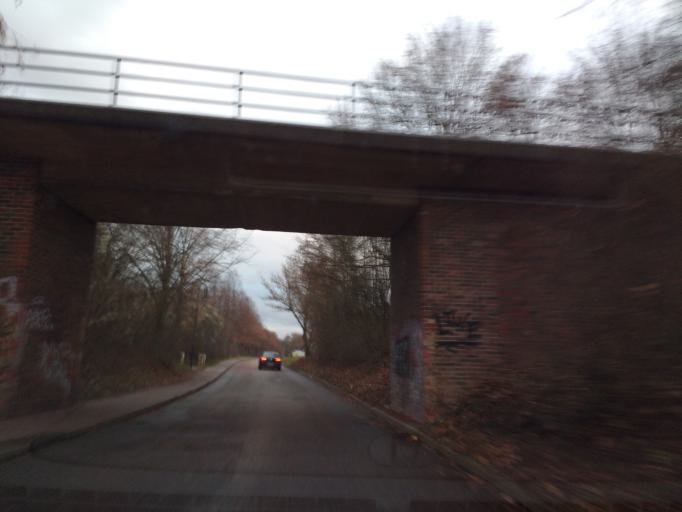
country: DE
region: Saxony-Anhalt
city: Braunsbedra
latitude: 51.2879
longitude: 11.8756
